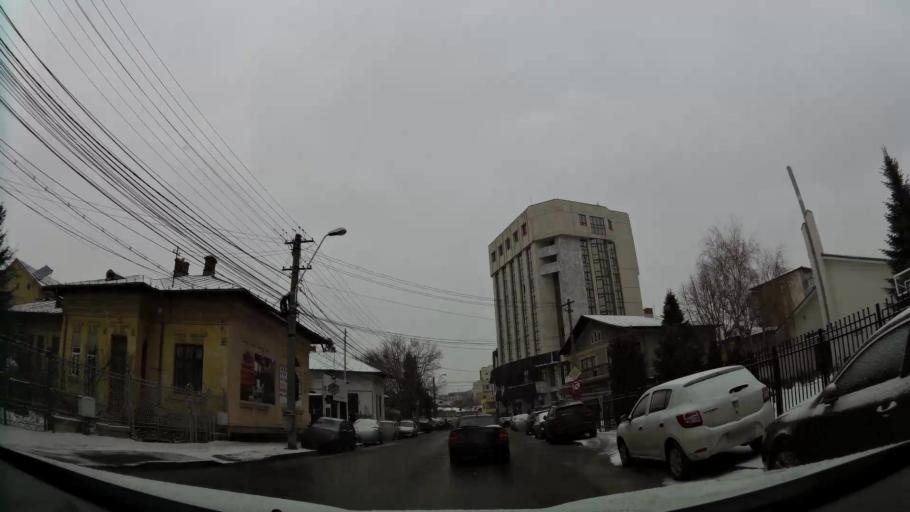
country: RO
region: Prahova
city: Ploiesti
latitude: 44.9363
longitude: 26.0212
